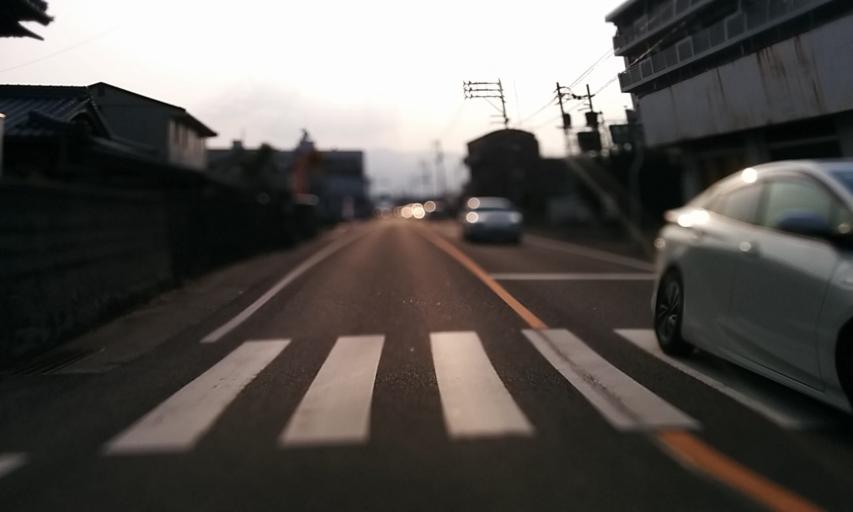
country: JP
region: Ehime
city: Saijo
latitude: 33.8971
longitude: 133.1142
